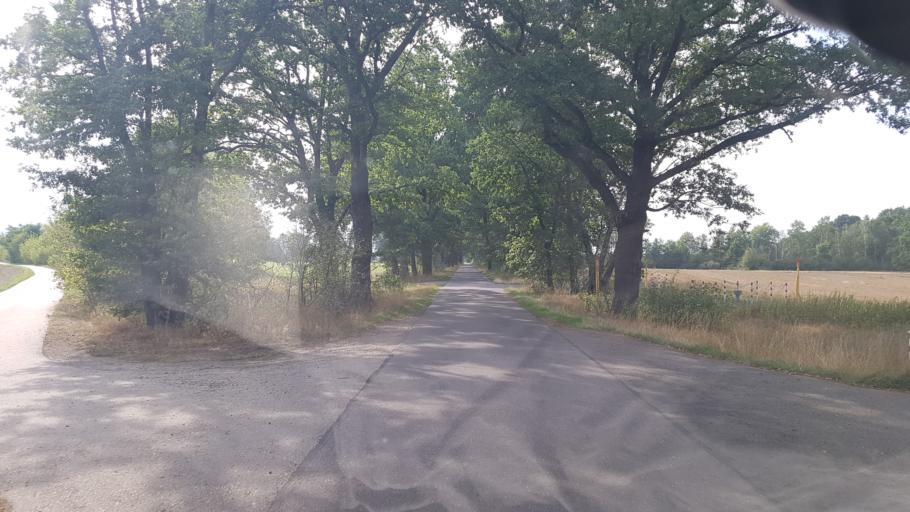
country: DE
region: Brandenburg
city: Plessa
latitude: 51.4407
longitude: 13.6045
